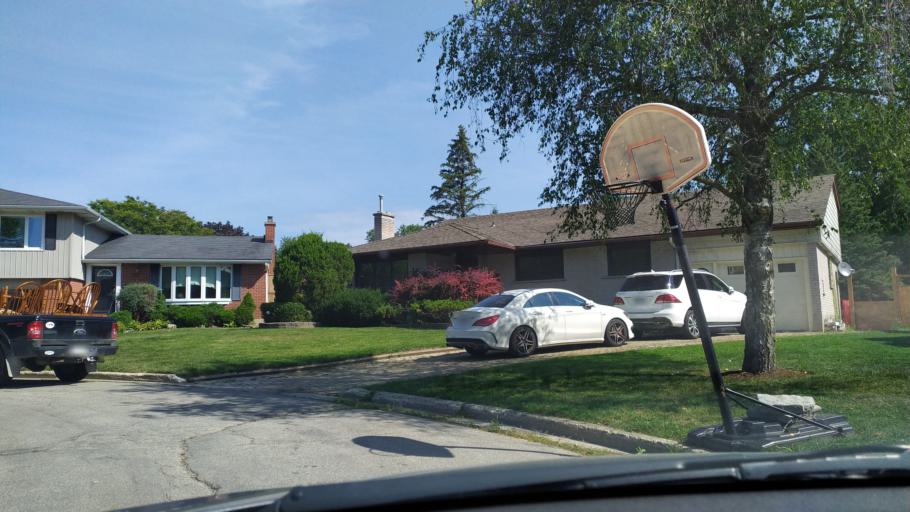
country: CA
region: Ontario
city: Stratford
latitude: 43.3797
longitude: -80.9651
